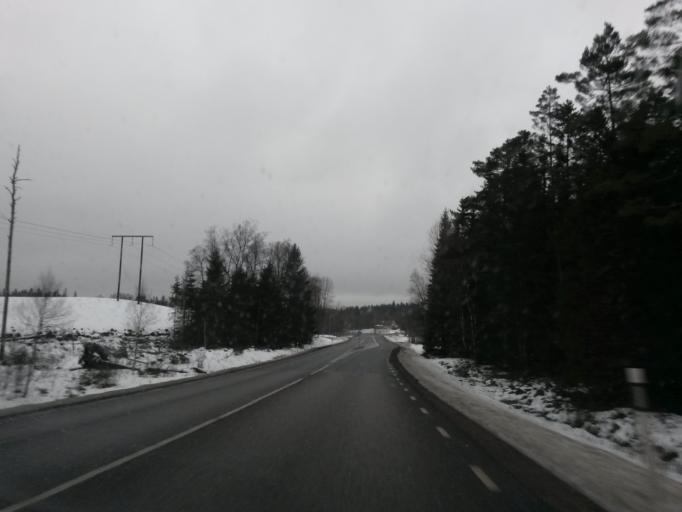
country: SE
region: Vaestra Goetaland
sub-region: Boras Kommun
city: Sandared
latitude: 57.7776
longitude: 12.7858
